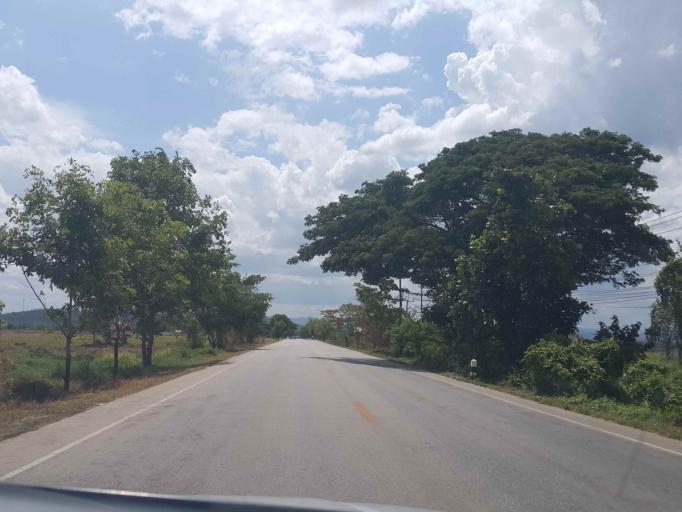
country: TH
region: Sukhothai
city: Thung Saliam
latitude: 17.3341
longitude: 99.6169
